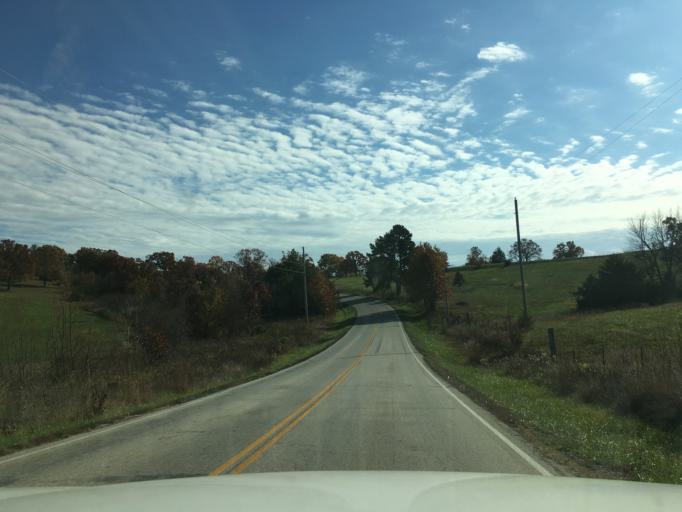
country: US
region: Missouri
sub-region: Maries County
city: Belle
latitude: 38.3269
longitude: -91.7605
